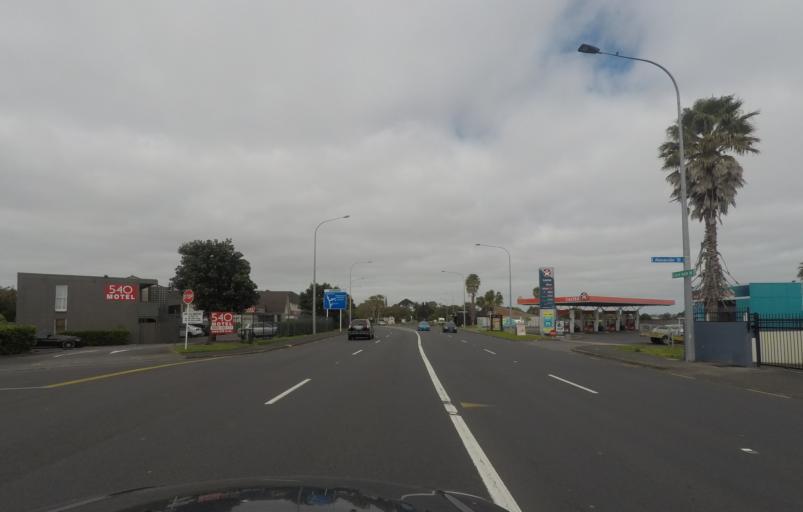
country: NZ
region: Auckland
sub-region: Auckland
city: Mangere
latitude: -36.9486
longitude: 174.8457
